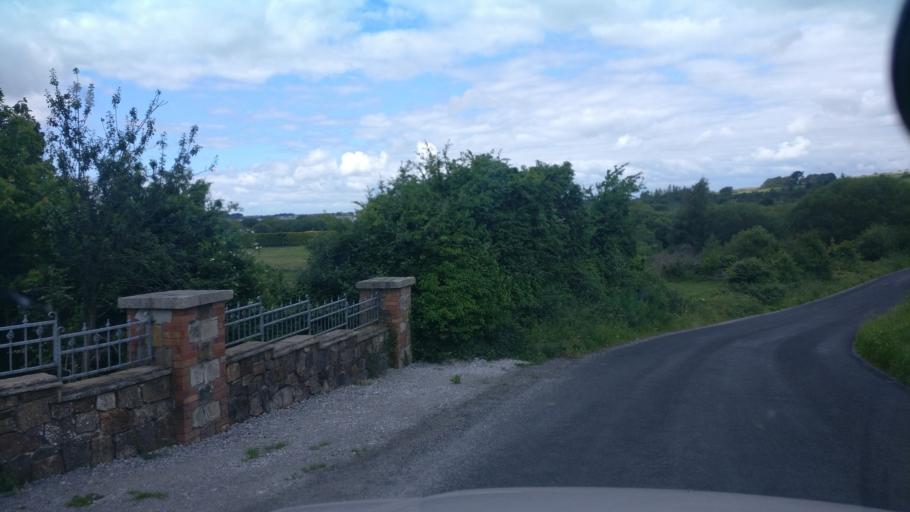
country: IE
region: Connaught
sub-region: County Galway
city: Loughrea
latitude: 53.1766
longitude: -8.5560
